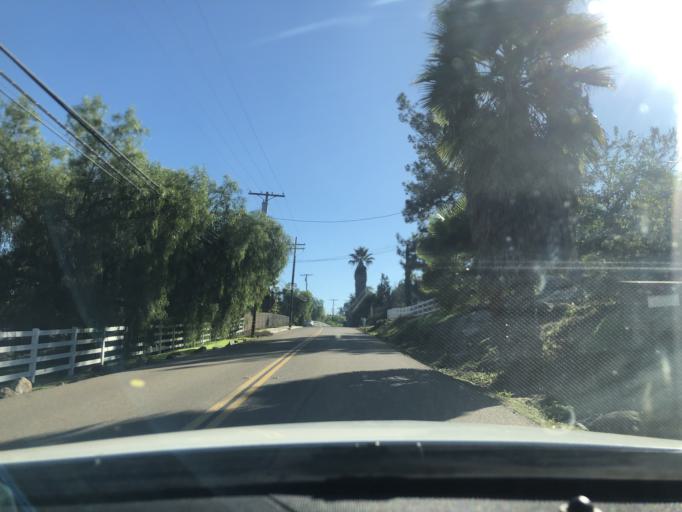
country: US
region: California
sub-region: San Diego County
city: El Cajon
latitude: 32.7788
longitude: -116.9475
